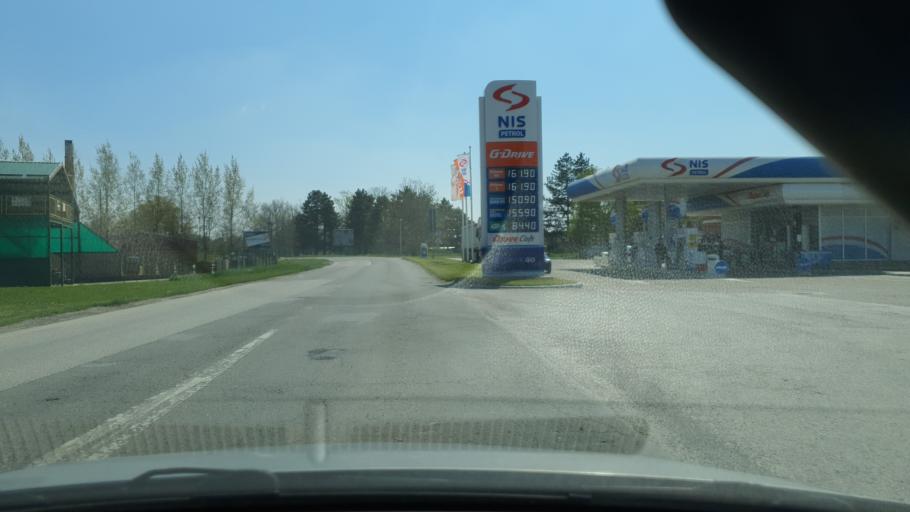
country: RS
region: Autonomna Pokrajina Vojvodina
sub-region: Zapadnobacki Okrug
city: Odzaci
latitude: 45.5154
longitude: 19.2480
